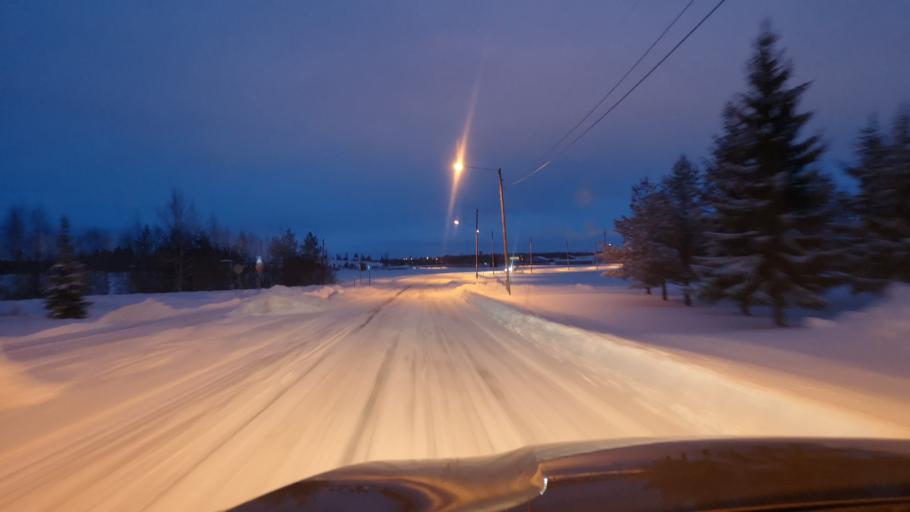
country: FI
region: Varsinais-Suomi
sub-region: Loimaa
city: Loimaa
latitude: 60.8636
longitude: 23.0815
